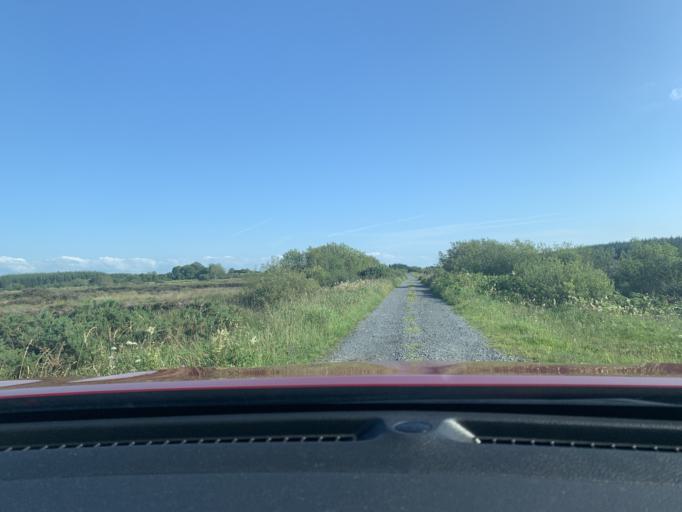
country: IE
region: Connaught
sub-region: Sligo
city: Tobercurry
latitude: 54.0693
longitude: -8.7957
